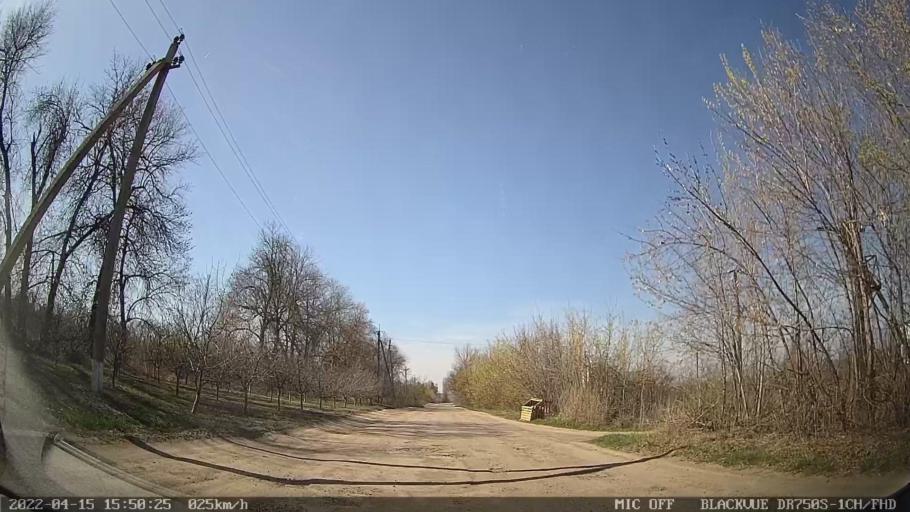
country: MD
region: Raionul Ocnita
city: Otaci
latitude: 48.3916
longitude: 27.9012
